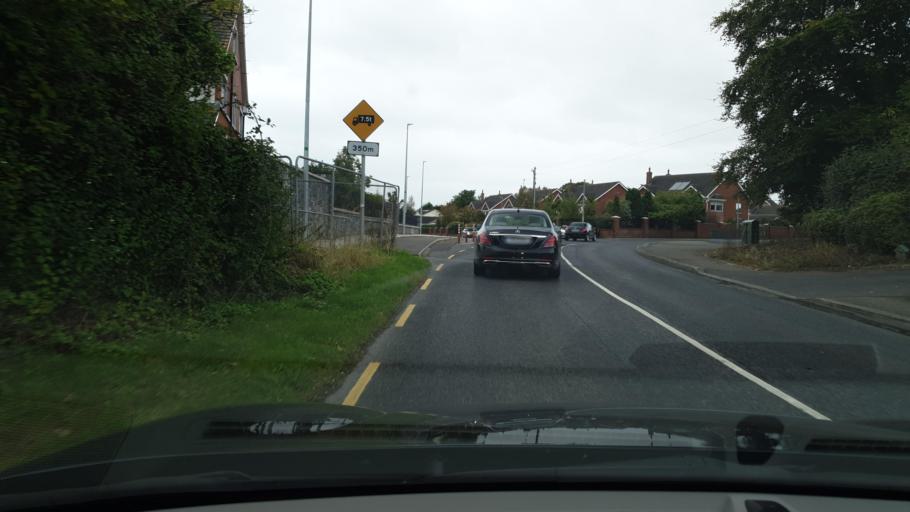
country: IE
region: Leinster
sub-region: An Mhi
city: Dunshaughlin
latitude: 53.5162
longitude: -6.5373
